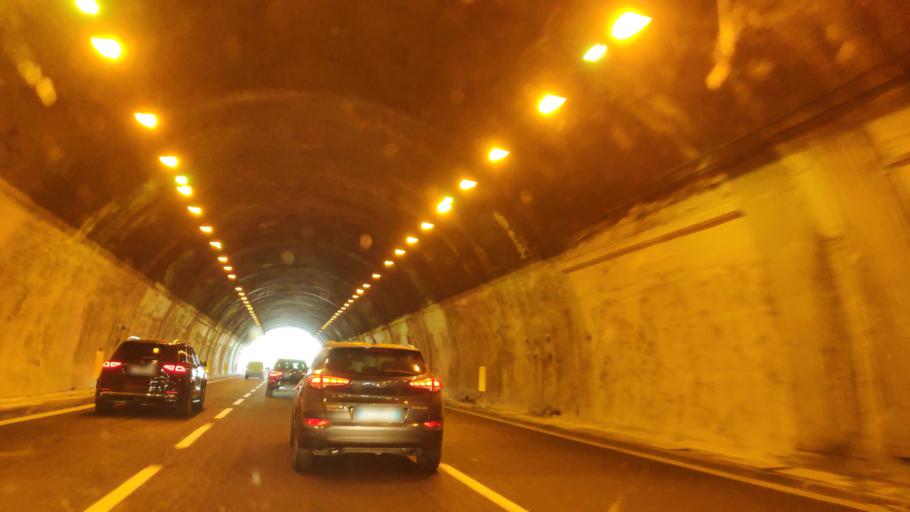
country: IT
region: Campania
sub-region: Provincia di Salerno
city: Mercato San Severino
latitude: 40.7708
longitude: 14.7412
